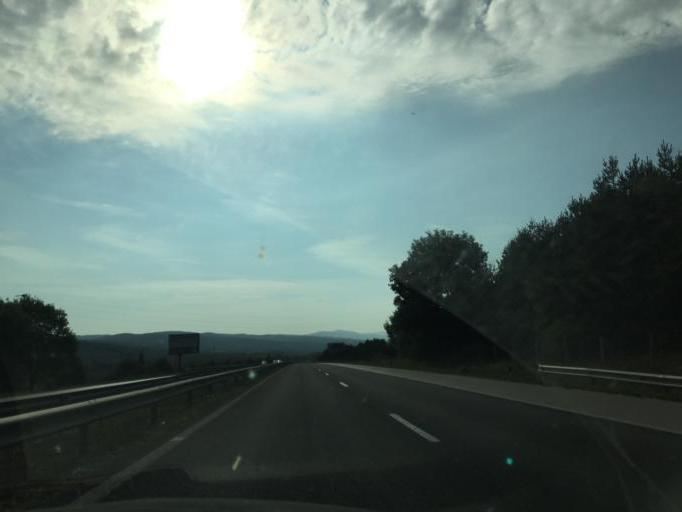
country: BG
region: Sofiya
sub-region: Obshtina Gorna Malina
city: Gorna Malina
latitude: 42.5476
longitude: 23.7080
